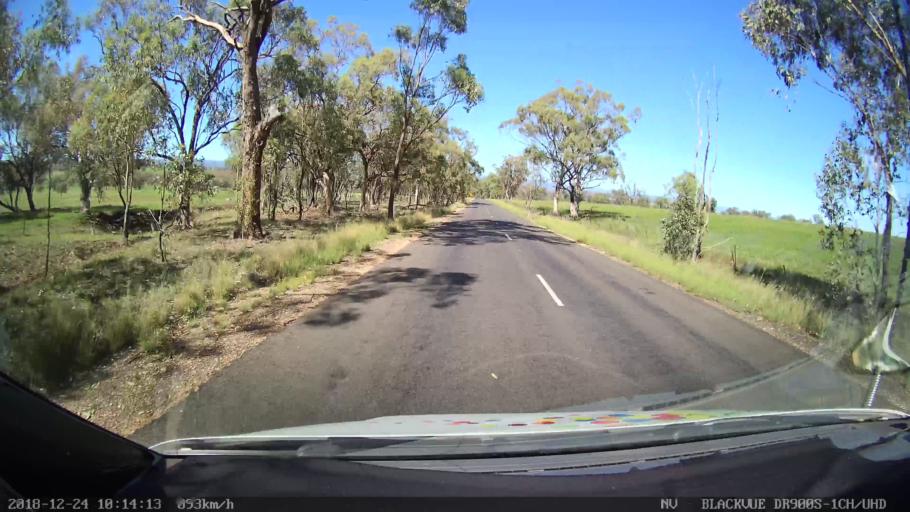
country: AU
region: New South Wales
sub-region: Liverpool Plains
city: Quirindi
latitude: -31.6959
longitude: 150.6311
